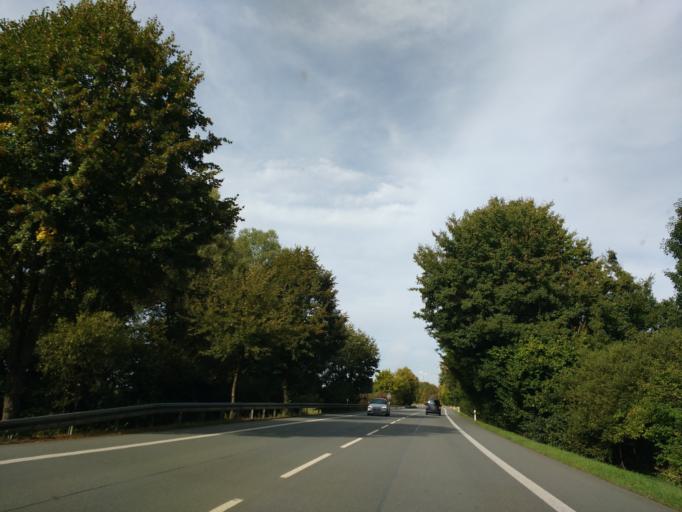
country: DE
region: North Rhine-Westphalia
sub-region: Regierungsbezirk Detmold
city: Nieheim
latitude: 51.7770
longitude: 9.1426
